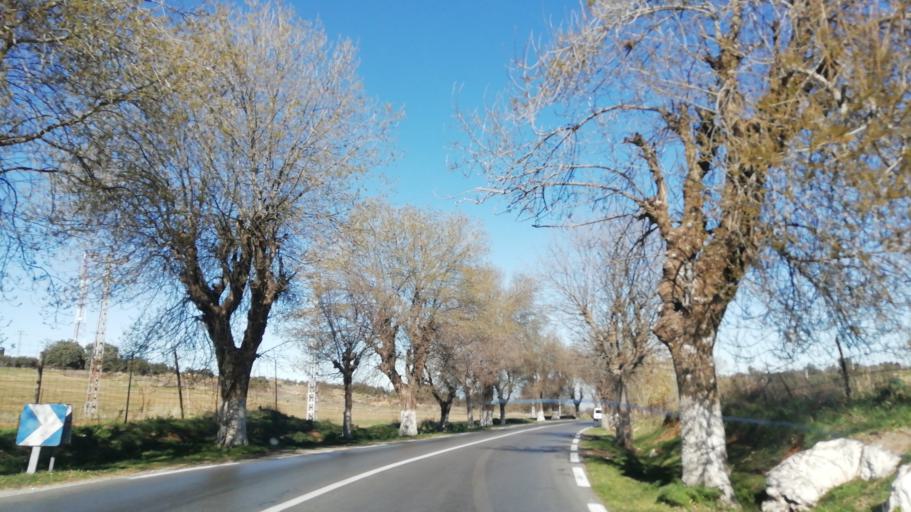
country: DZ
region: Tlemcen
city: Mansoura
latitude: 34.8346
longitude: -1.3727
